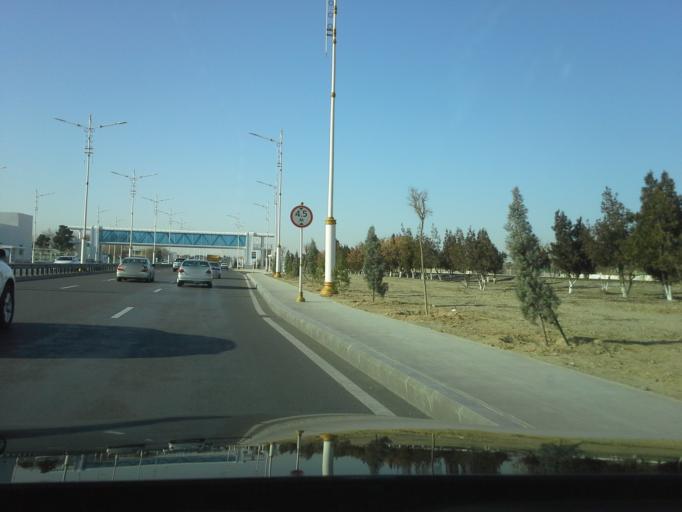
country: TM
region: Ahal
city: Ashgabat
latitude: 37.9585
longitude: 58.3677
